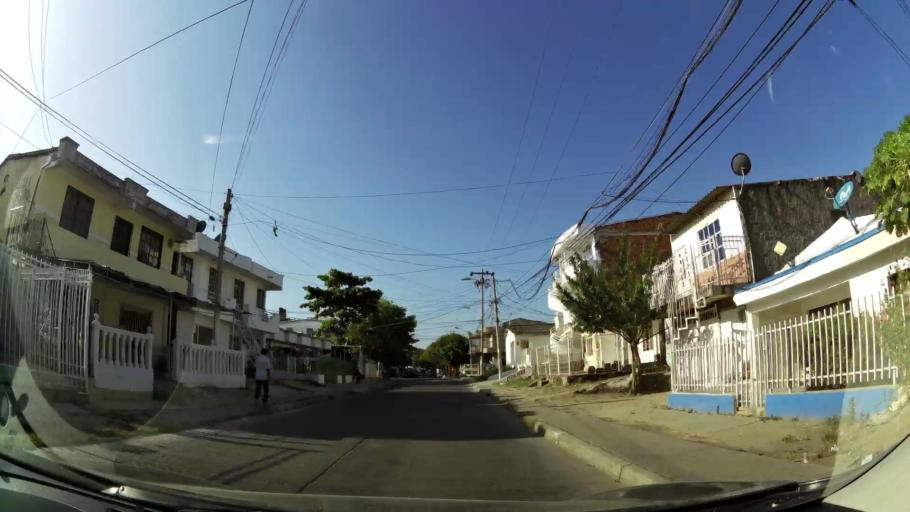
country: CO
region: Bolivar
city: Cartagena
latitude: 10.3978
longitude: -75.4995
